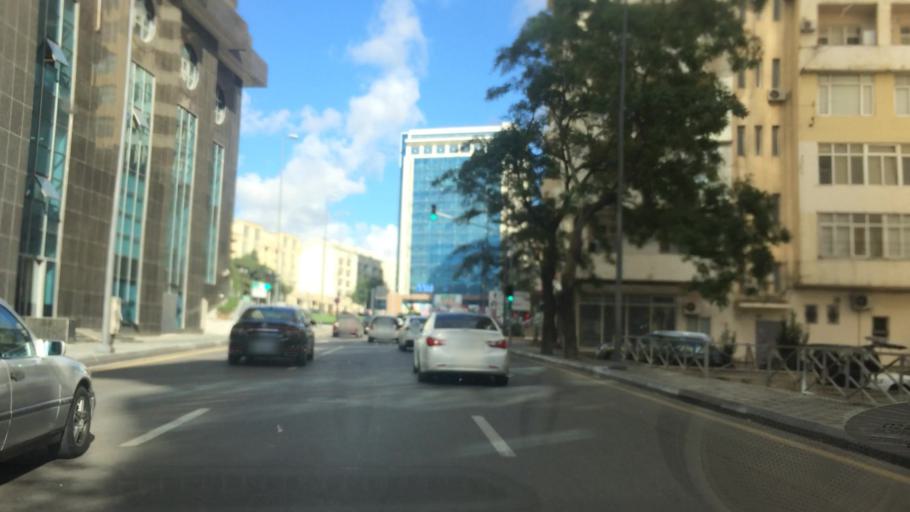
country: AZ
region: Baki
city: Badamdar
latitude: 40.3821
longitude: 49.8240
